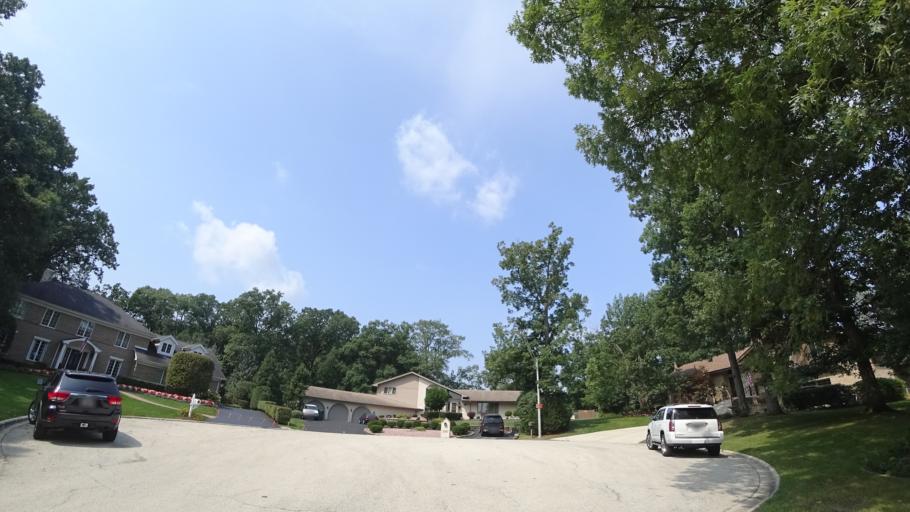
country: US
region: Illinois
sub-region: Cook County
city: Orland Park
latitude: 41.6216
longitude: -87.8719
